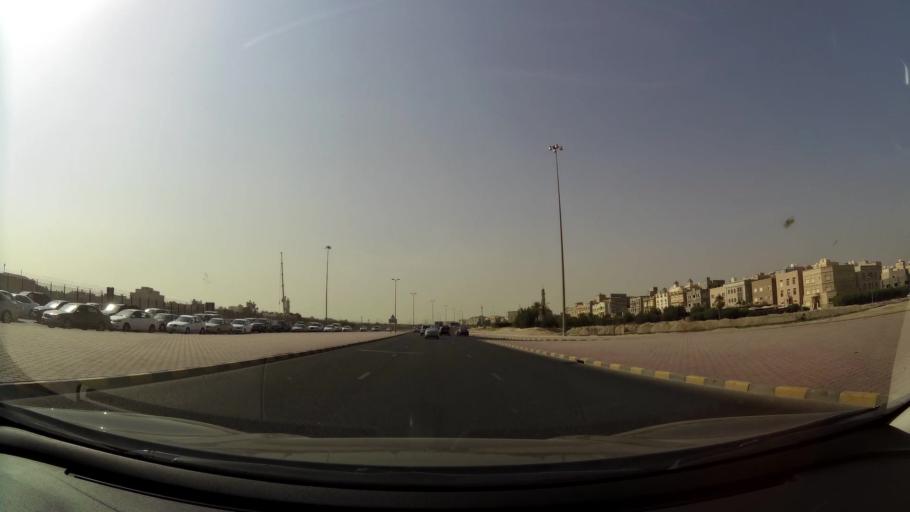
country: KW
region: Al Ahmadi
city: Al Manqaf
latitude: 29.1196
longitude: 48.1160
